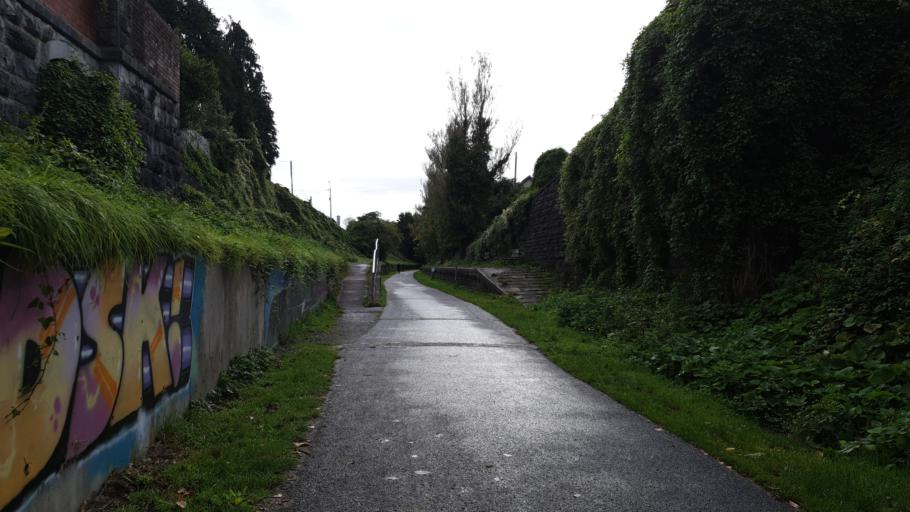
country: IE
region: Munster
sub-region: County Cork
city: Cork
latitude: 51.8965
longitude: -8.4192
